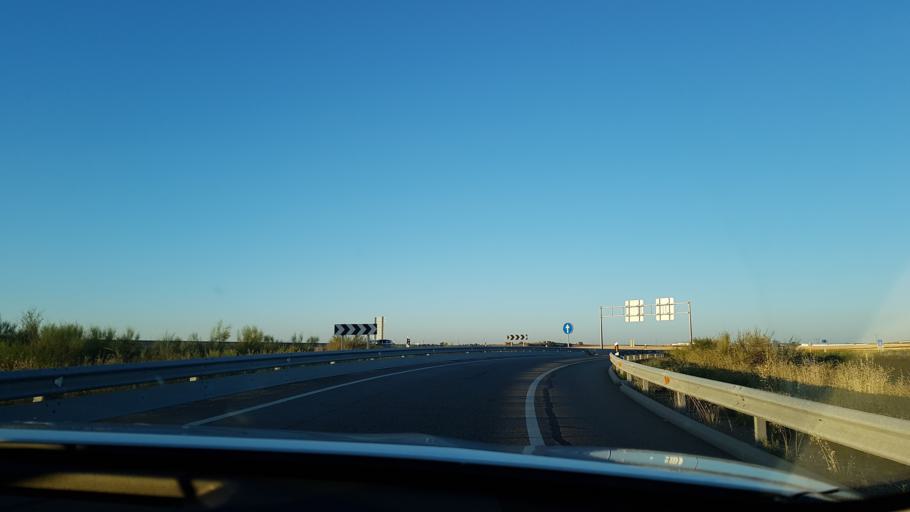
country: ES
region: Castille and Leon
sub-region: Provincia de Zamora
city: Valcabado
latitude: 41.5563
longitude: -5.7514
